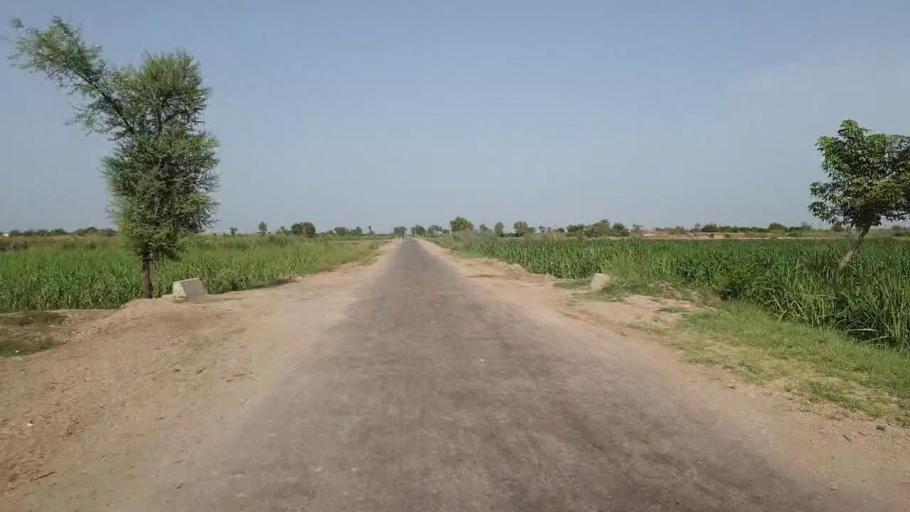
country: PK
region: Sindh
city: Sakrand
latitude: 26.2842
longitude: 68.2576
